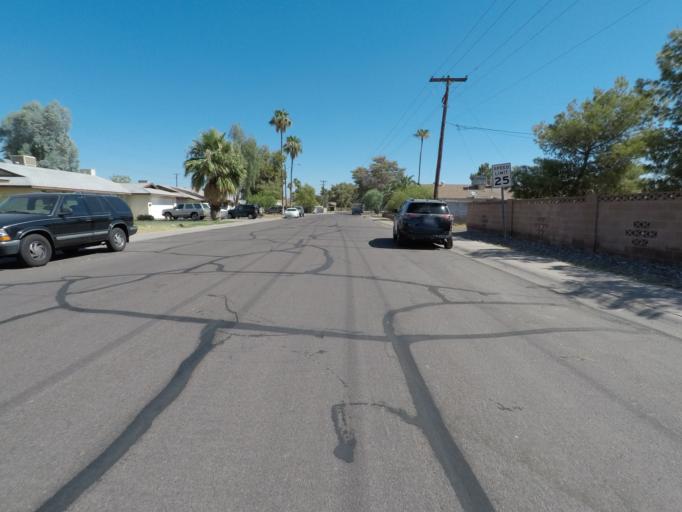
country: US
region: Arizona
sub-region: Maricopa County
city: Tempe Junction
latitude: 33.3987
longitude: -111.9426
